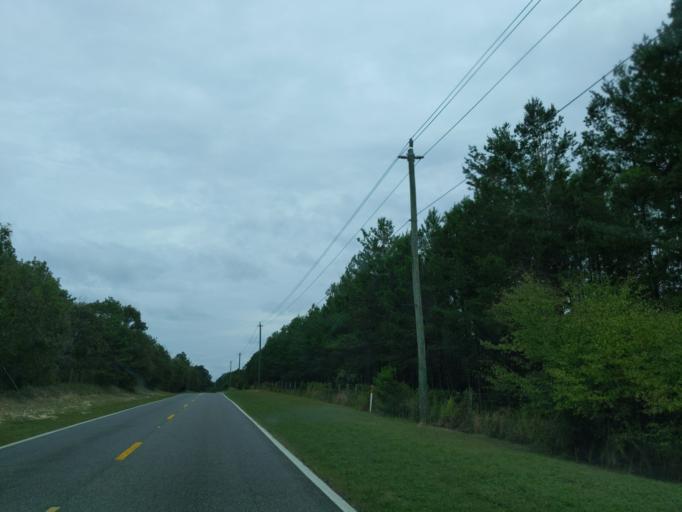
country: US
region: Florida
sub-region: Leon County
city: Woodville
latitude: 30.3699
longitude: -84.1861
